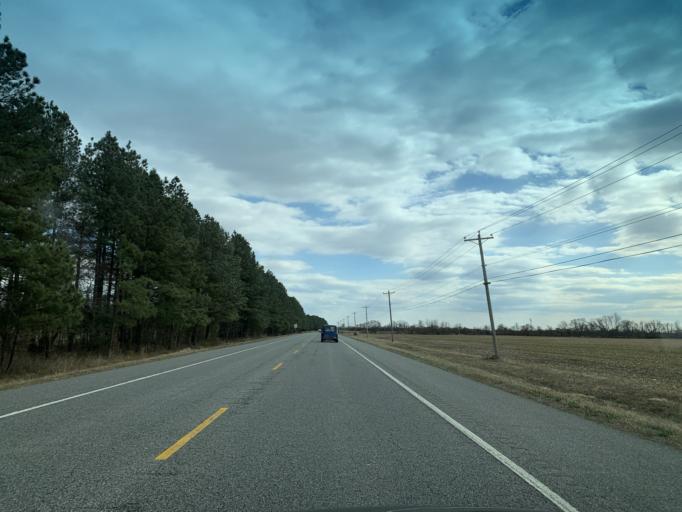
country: US
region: Maryland
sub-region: Queen Anne's County
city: Centreville
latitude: 38.9841
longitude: -76.0716
